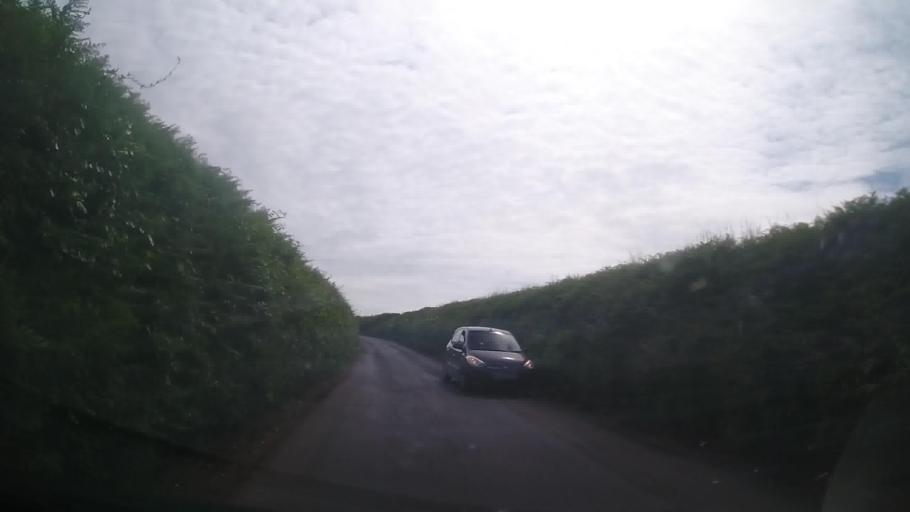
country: GB
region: England
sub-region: Devon
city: Salcombe
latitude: 50.2523
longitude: -3.6820
